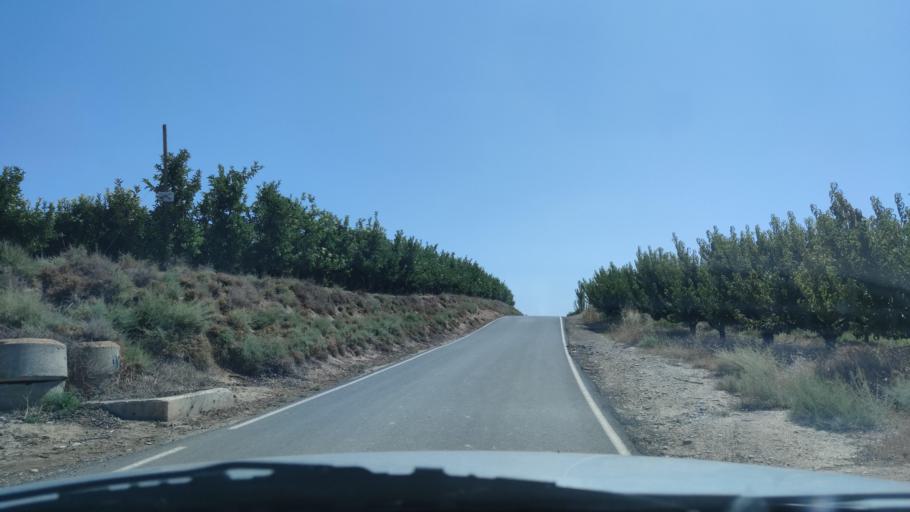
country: ES
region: Catalonia
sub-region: Provincia de Lleida
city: Alpicat
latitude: 41.6701
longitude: 0.5635
